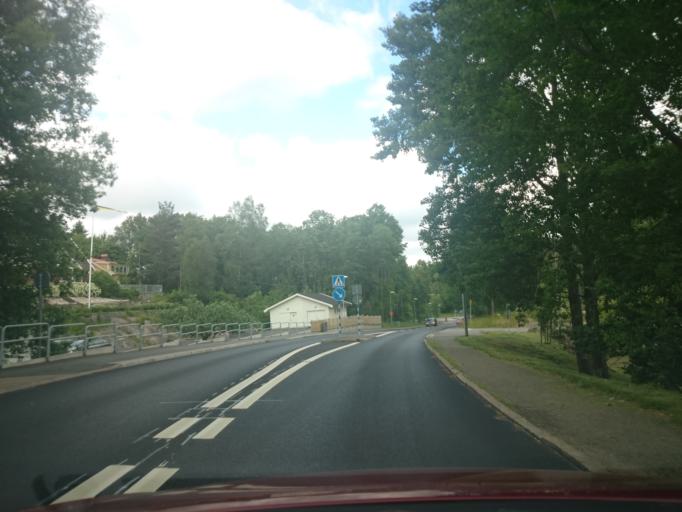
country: SE
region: Vaestra Goetaland
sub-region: Molndal
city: Moelndal
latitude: 57.6700
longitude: 12.0566
